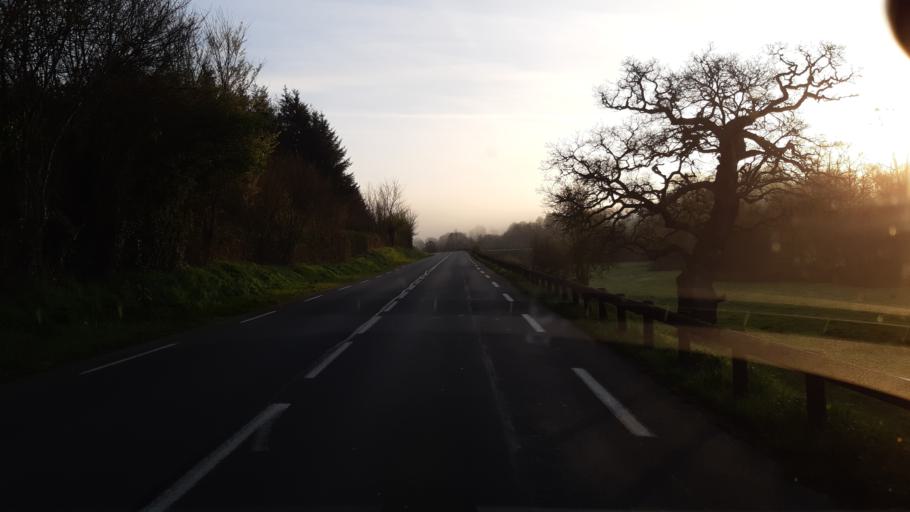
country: FR
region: Lower Normandy
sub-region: Departement de la Manche
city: Agneaux
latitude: 49.0803
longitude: -1.1202
